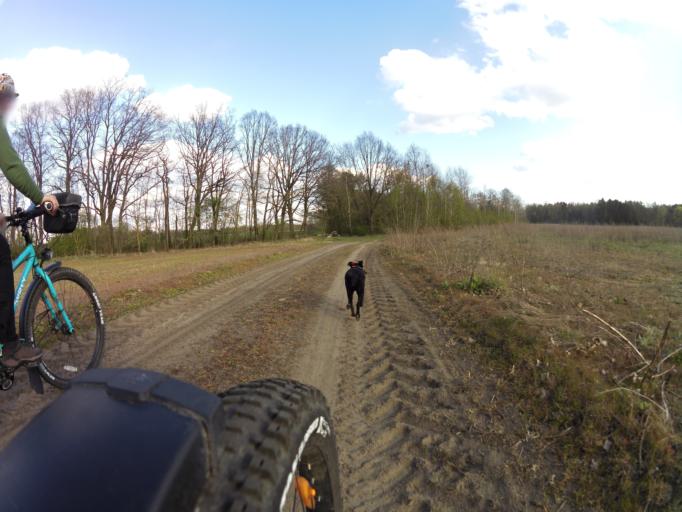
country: PL
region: West Pomeranian Voivodeship
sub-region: Powiat gryficki
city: Ploty
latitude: 53.7682
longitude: 15.2546
